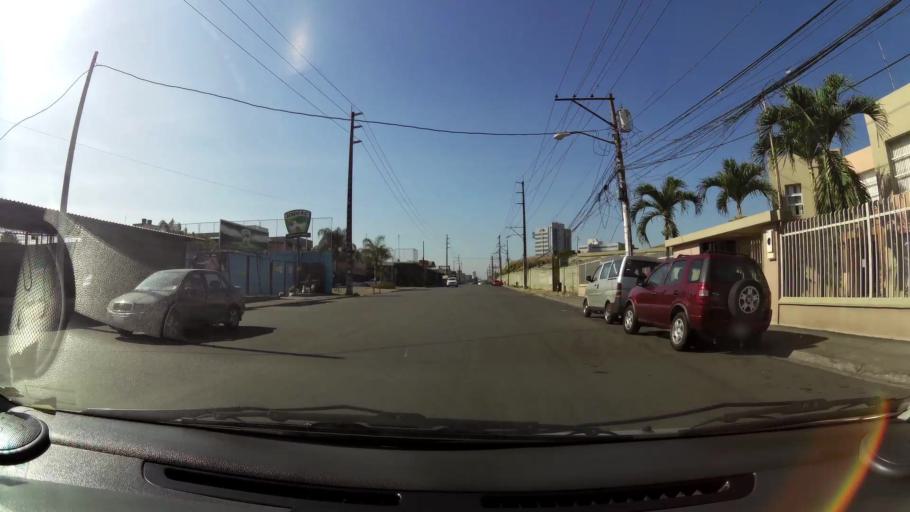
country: EC
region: Guayas
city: Eloy Alfaro
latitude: -2.1547
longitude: -79.8990
